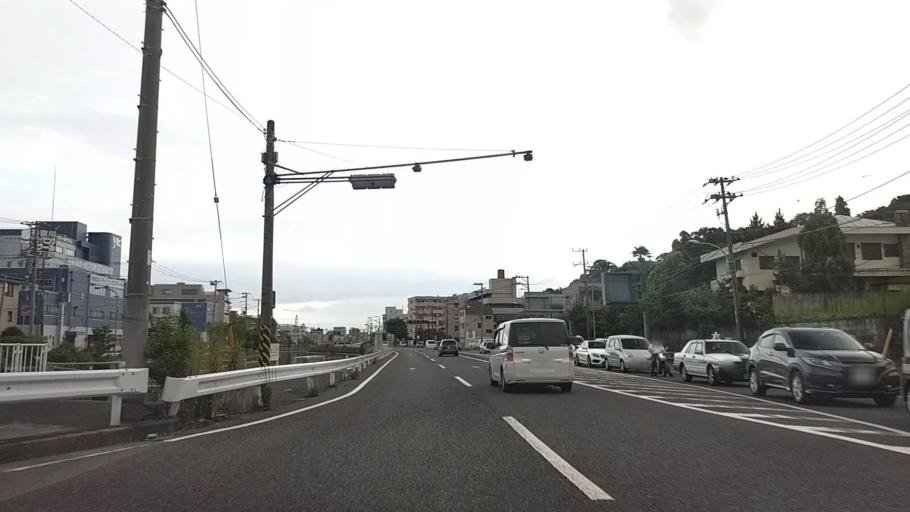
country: JP
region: Kanagawa
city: Yokohama
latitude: 35.4304
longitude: 139.6208
